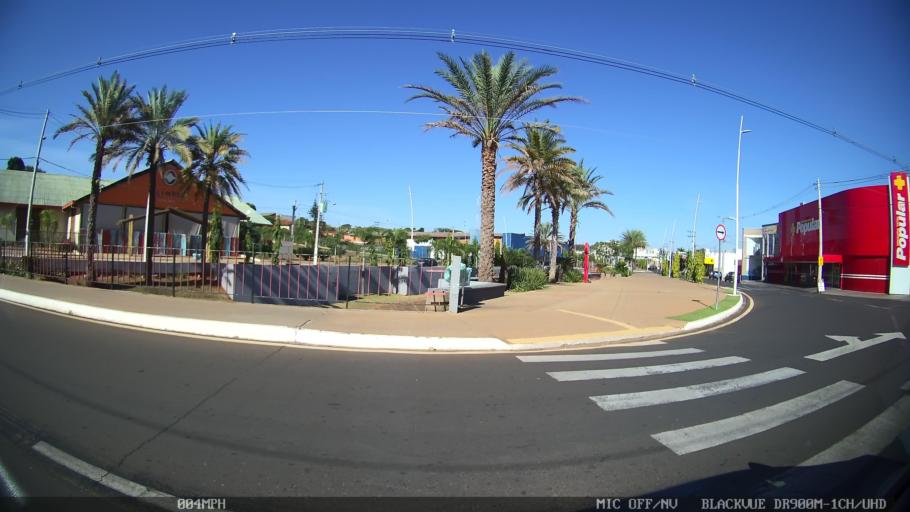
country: BR
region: Sao Paulo
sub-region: Olimpia
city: Olimpia
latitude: -20.7292
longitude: -48.9149
